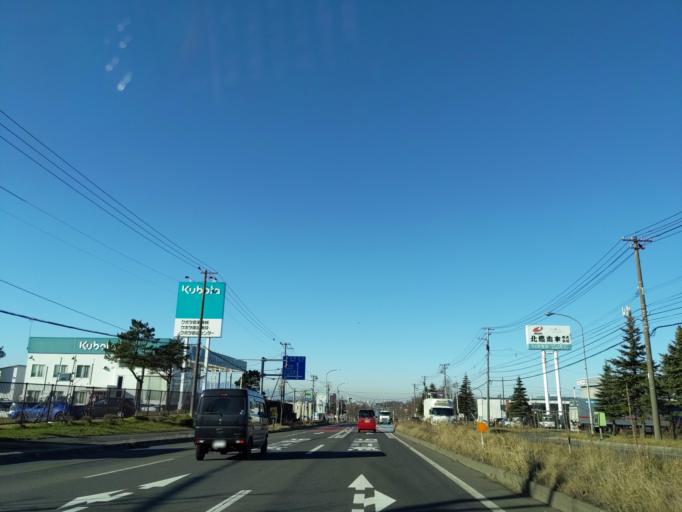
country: JP
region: Hokkaido
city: Kitahiroshima
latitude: 42.9626
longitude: 141.4897
